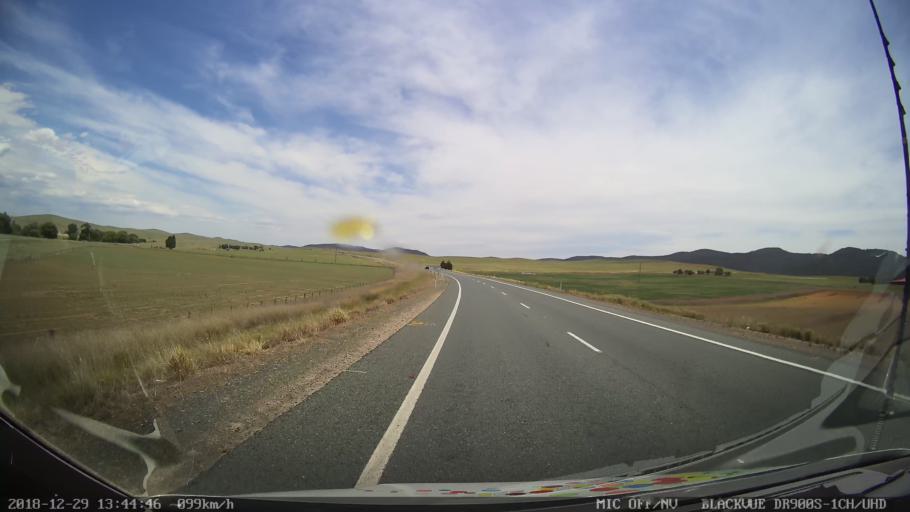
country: AU
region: New South Wales
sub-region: Cooma-Monaro
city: Cooma
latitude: -36.0867
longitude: 149.1474
